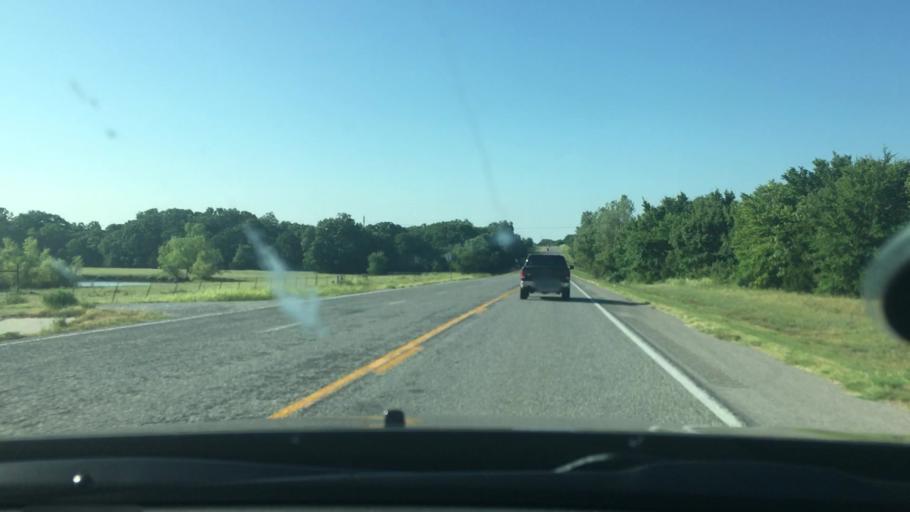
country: US
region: Oklahoma
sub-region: Johnston County
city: Tishomingo
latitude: 34.2711
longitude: -96.7745
